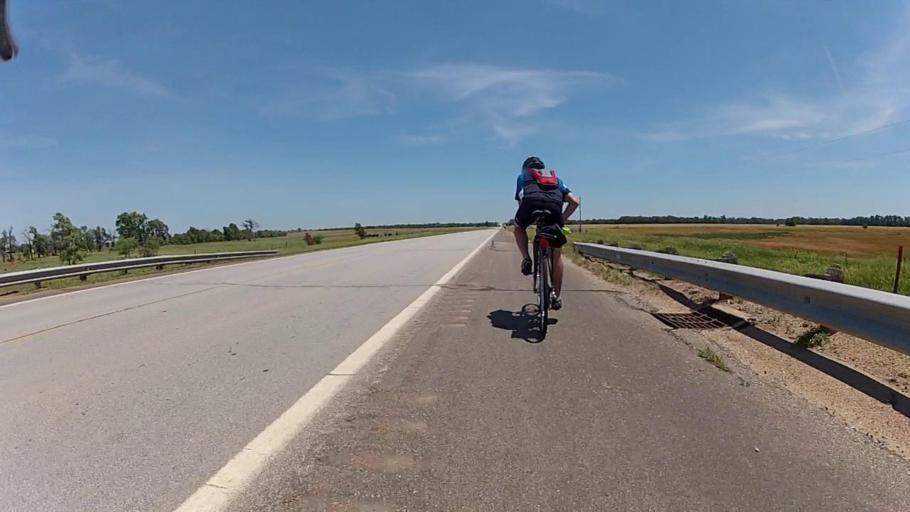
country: US
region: Kansas
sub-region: Barber County
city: Medicine Lodge
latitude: 37.2533
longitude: -98.3152
